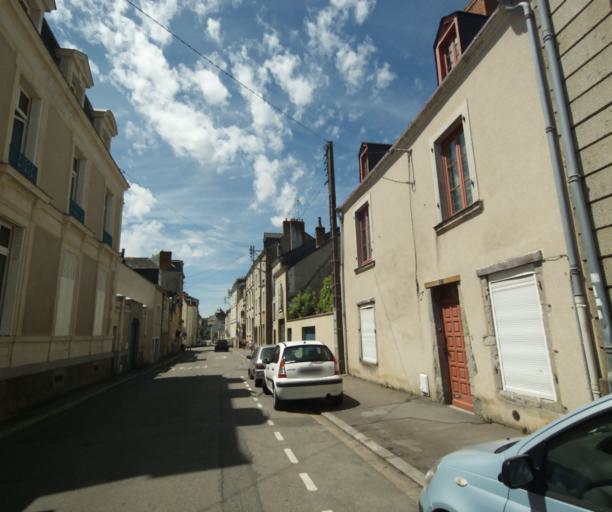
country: FR
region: Pays de la Loire
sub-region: Departement de la Mayenne
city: Laval
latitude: 48.0673
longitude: -0.7635
